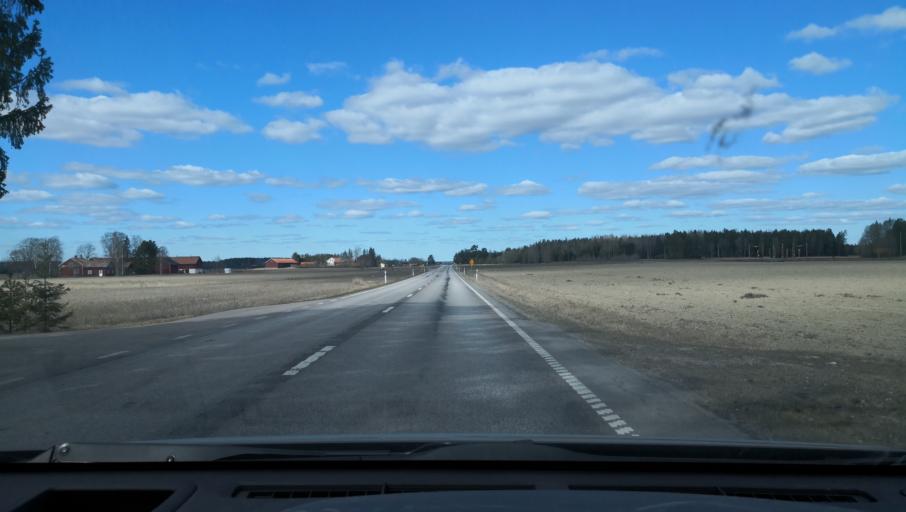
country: SE
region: Vaestmanland
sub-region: Sala Kommun
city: Sala
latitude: 59.8661
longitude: 16.6295
